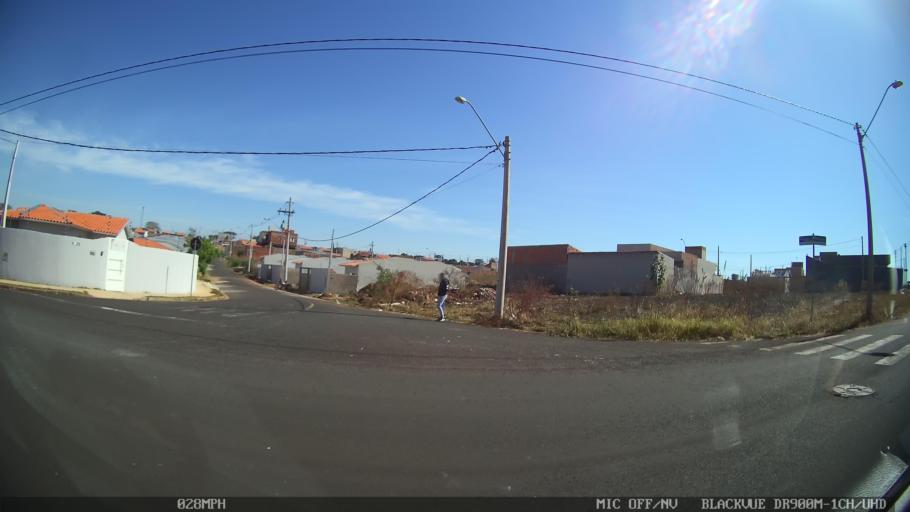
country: BR
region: Sao Paulo
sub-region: Sao Jose Do Rio Preto
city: Sao Jose do Rio Preto
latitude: -20.7514
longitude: -49.4224
